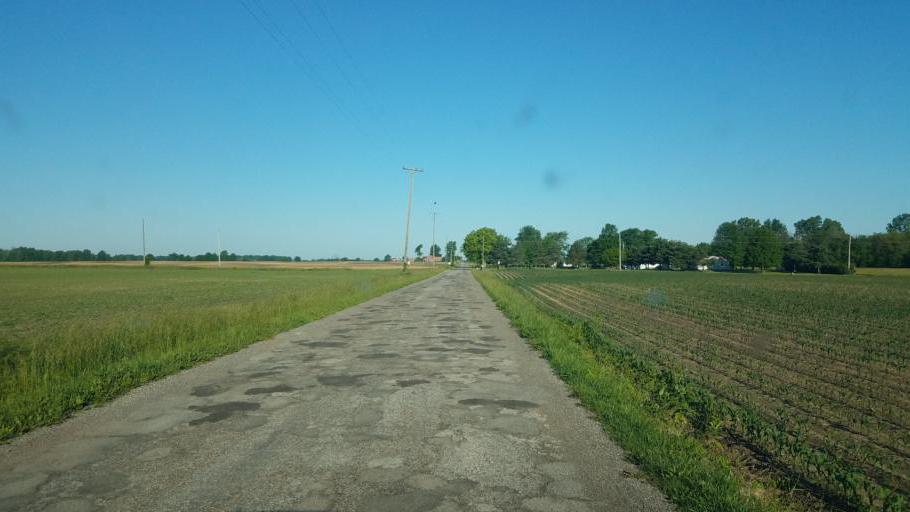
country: US
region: Ohio
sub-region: Morrow County
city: Mount Gilead
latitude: 40.6160
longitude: -82.8976
